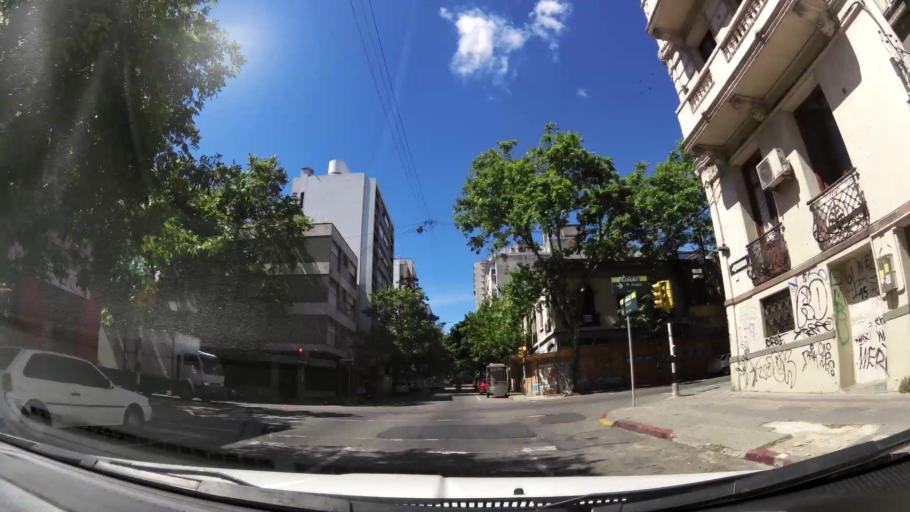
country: UY
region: Montevideo
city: Montevideo
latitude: -34.9027
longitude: -56.1884
